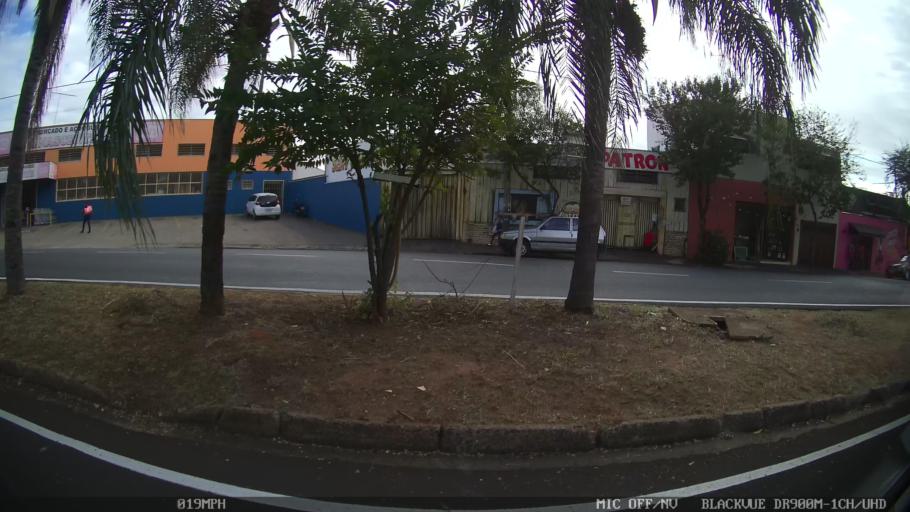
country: BR
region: Sao Paulo
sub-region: Sao Jose Do Rio Preto
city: Sao Jose do Rio Preto
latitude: -20.8395
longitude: -49.3751
